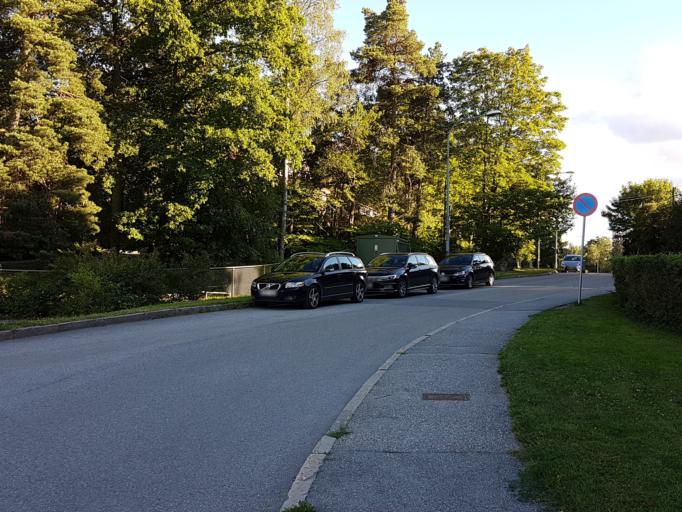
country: SE
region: Stockholm
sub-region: Sundbybergs Kommun
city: Sundbyberg
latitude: 59.3269
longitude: 17.9723
